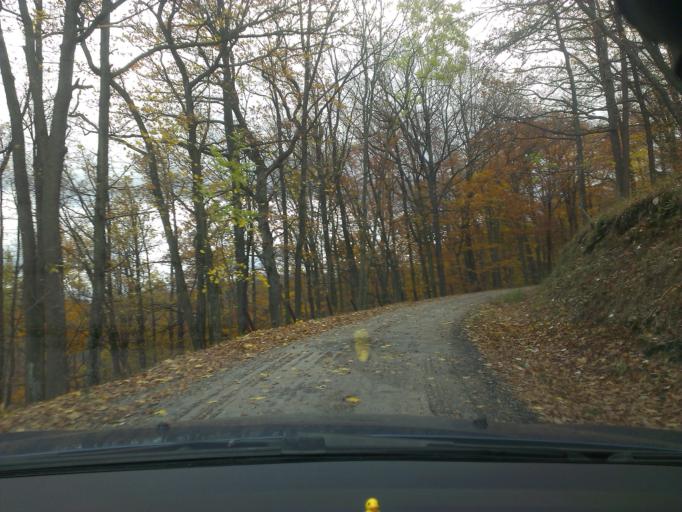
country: SK
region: Trnavsky
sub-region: Okres Trnava
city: Piestany
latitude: 48.6140
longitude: 17.9481
